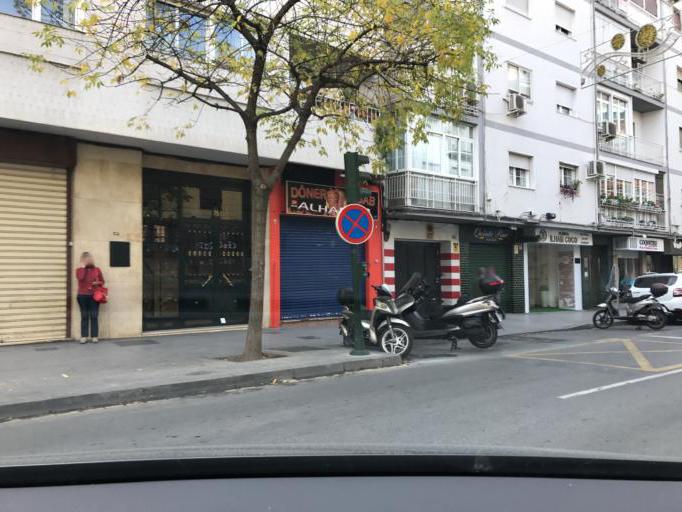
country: ES
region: Andalusia
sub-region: Provincia de Granada
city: Granada
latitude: 37.1691
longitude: -3.6030
